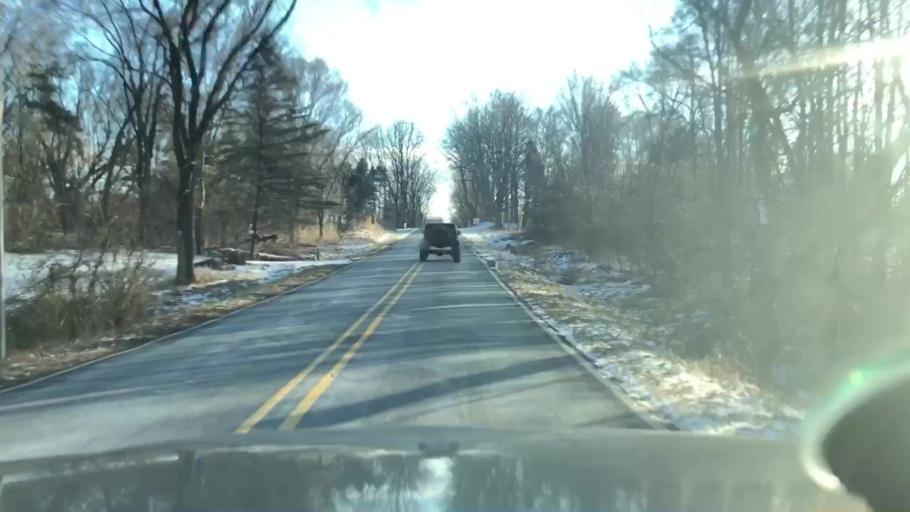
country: US
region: Michigan
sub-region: Jackson County
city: Vandercook Lake
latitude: 42.1351
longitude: -84.4517
